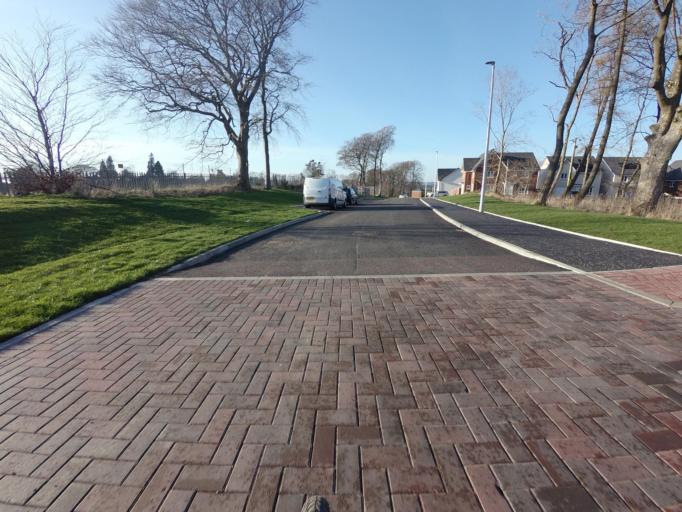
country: GB
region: Scotland
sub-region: West Lothian
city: West Calder
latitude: 55.8617
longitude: -3.5382
